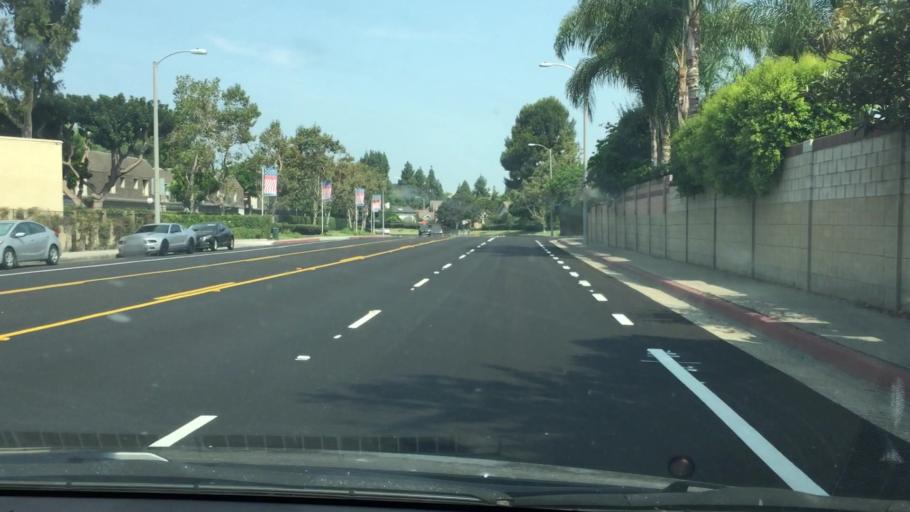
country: US
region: California
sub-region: Orange County
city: Costa Mesa
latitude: 33.6897
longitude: -117.9049
